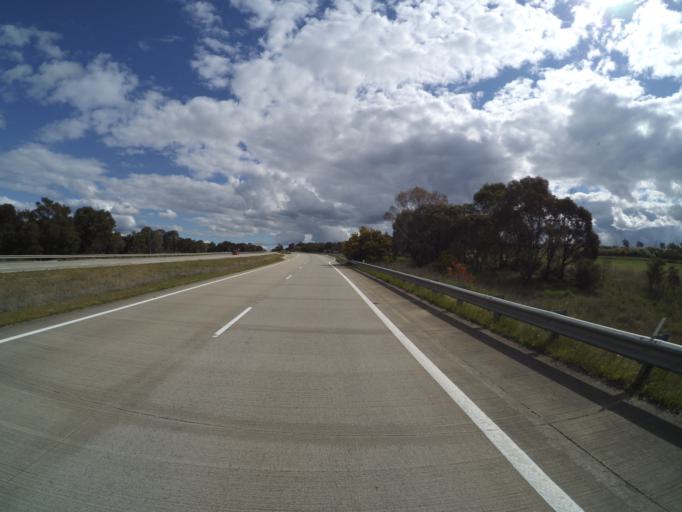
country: AU
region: New South Wales
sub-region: Yass Valley
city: Murrumbateman
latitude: -34.7925
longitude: 149.1687
